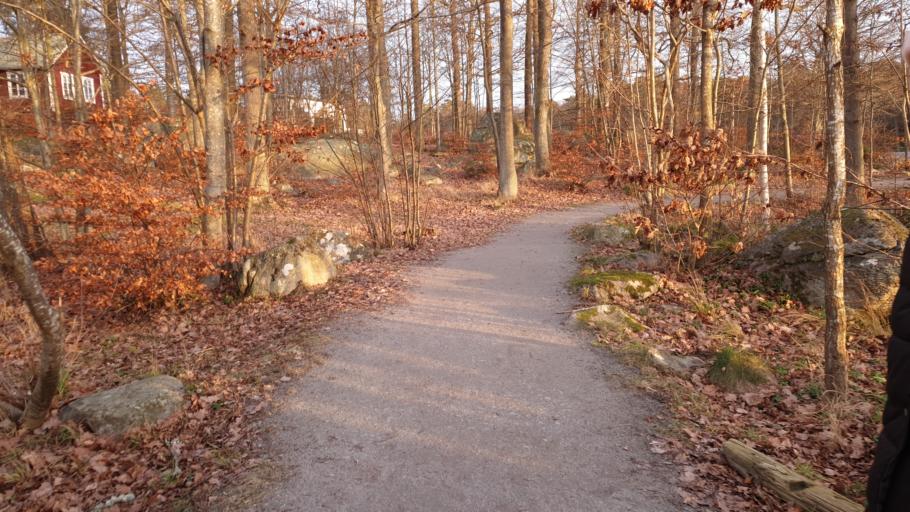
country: SE
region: Blekinge
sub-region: Karlshamns Kommun
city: Karlshamn
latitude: 56.1617
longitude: 14.8771
